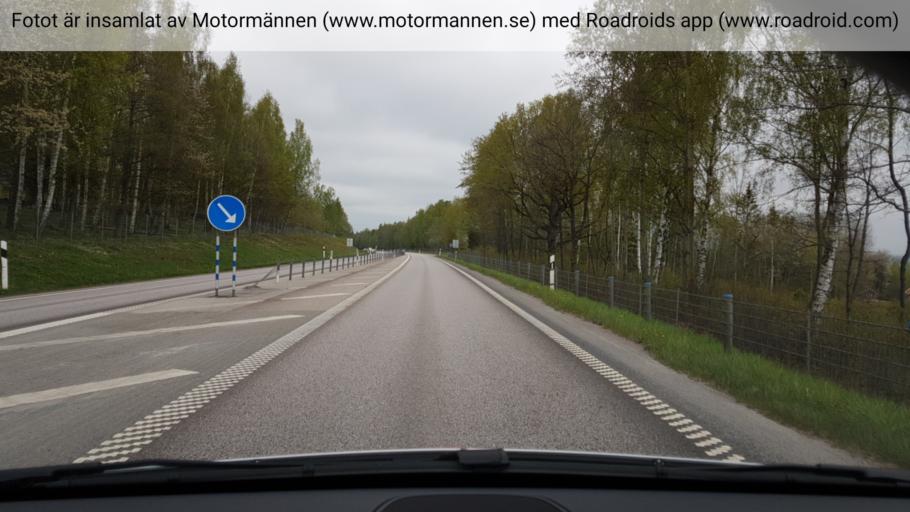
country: SE
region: Vaestra Goetaland
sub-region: Skovde Kommun
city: Stopen
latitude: 58.4856
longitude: 13.8520
